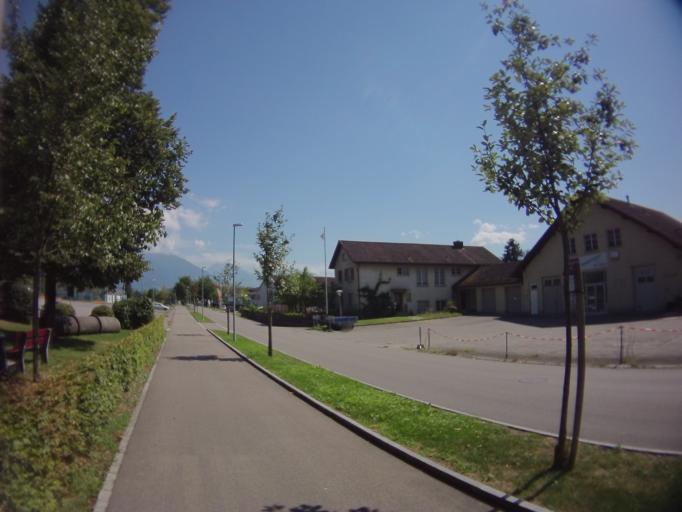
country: CH
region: Saint Gallen
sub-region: Wahlkreis See-Gaster
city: Uznach
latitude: 47.2231
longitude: 8.9824
